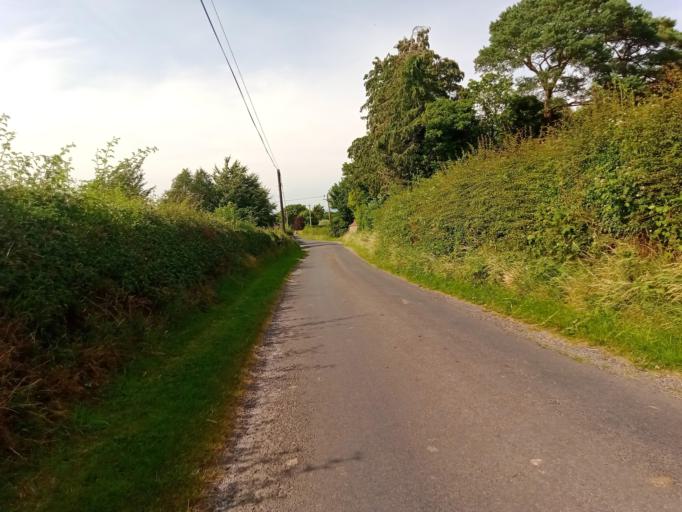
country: IE
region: Leinster
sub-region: Laois
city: Rathdowney
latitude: 52.8112
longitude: -7.4695
